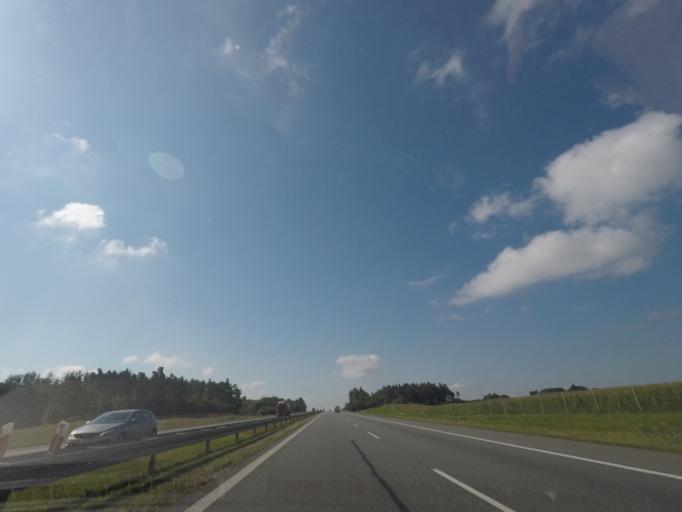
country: PL
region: Pomeranian Voivodeship
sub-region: Powiat tczewski
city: Subkowy
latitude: 54.0521
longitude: 18.6715
